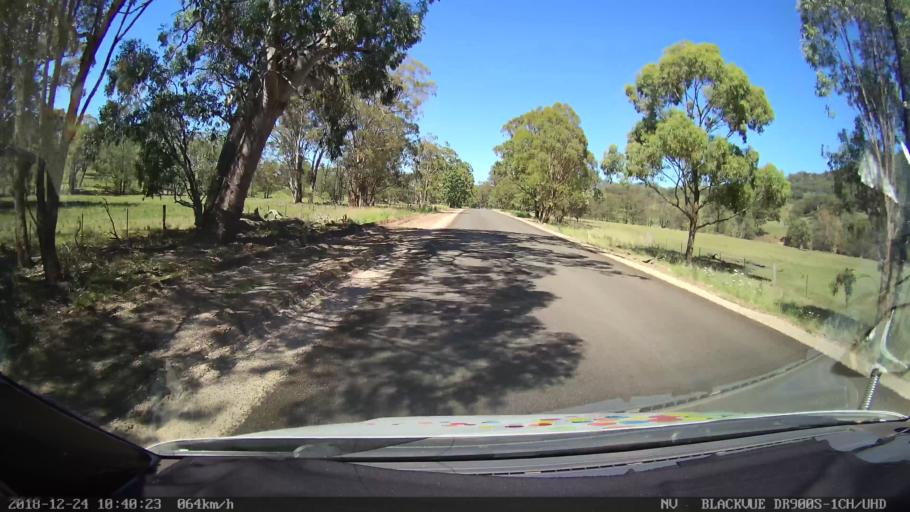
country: AU
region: New South Wales
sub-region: Upper Hunter Shire
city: Merriwa
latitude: -31.8614
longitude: 150.4677
